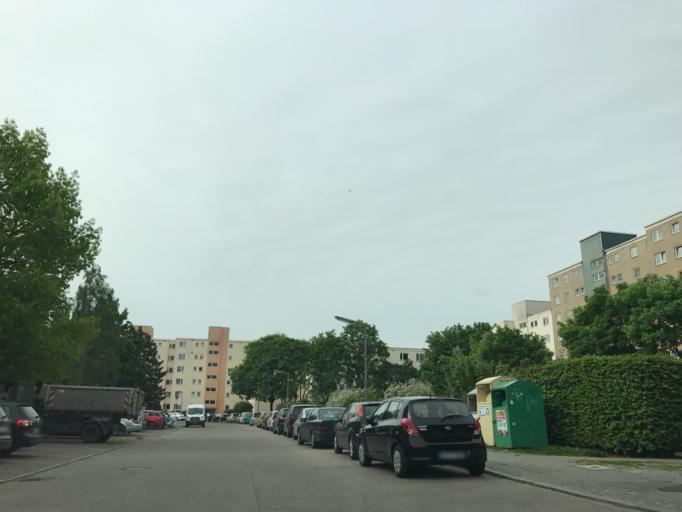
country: DE
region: Berlin
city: Staaken
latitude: 52.5319
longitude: 13.1460
